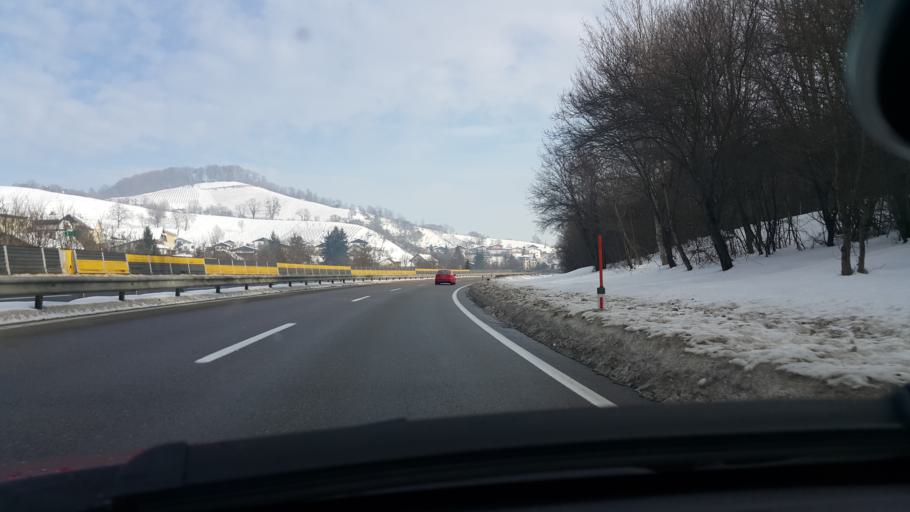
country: SI
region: Maribor
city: Maribor
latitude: 46.5769
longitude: 15.6587
